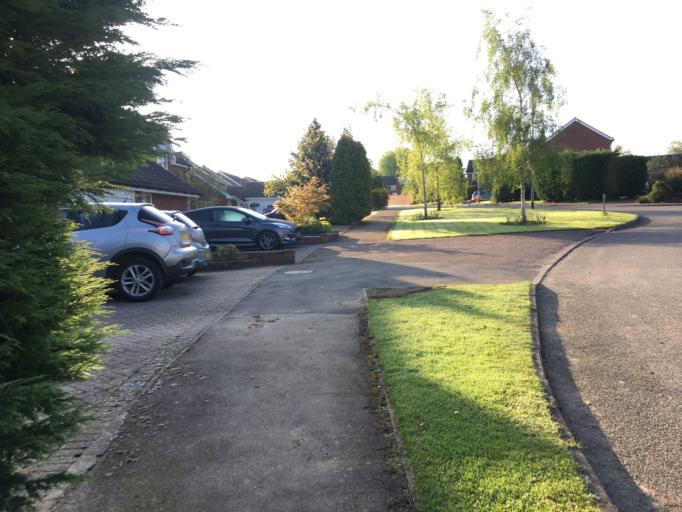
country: GB
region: England
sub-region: Leicestershire
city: Houghton on the Hill
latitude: 52.6267
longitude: -1.0031
